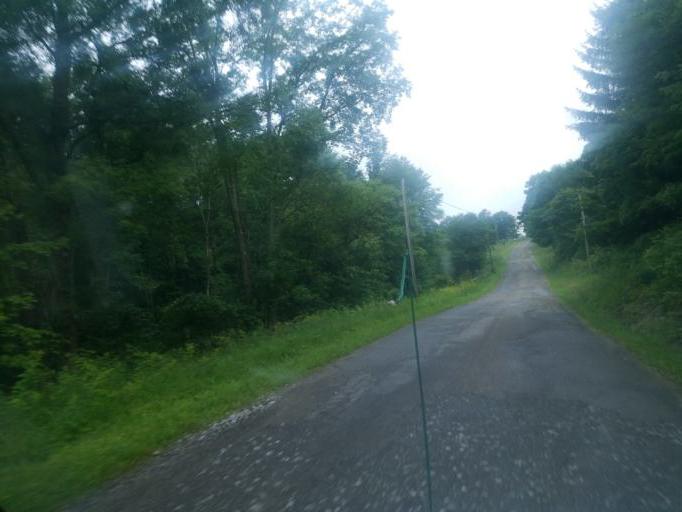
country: US
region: Ohio
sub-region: Columbiana County
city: Salineville
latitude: 40.6048
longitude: -80.9128
